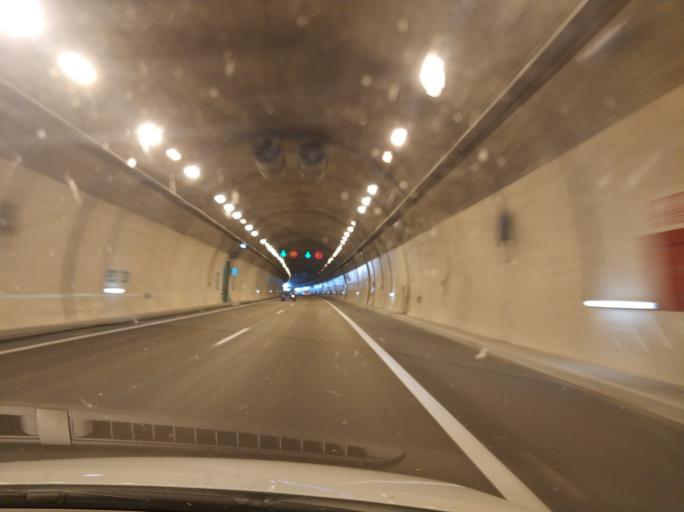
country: ES
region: Castille and Leon
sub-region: Provincia de Burgos
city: Burgos
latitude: 42.3811
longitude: -3.6681
